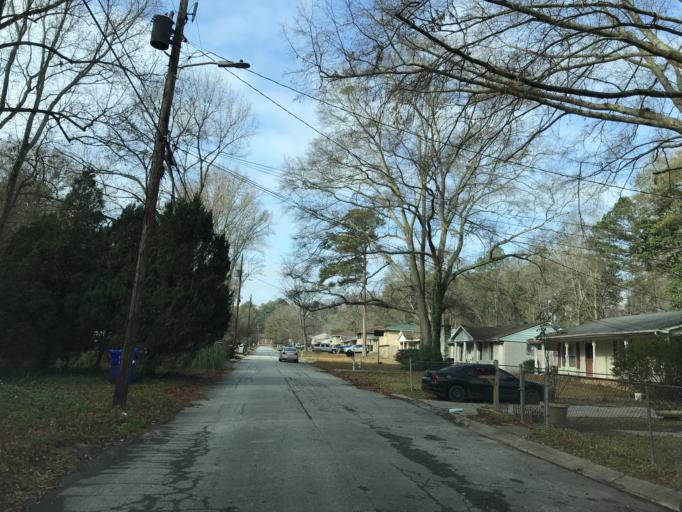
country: US
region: Georgia
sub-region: Clayton County
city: Morrow
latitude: 33.5612
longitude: -84.3644
